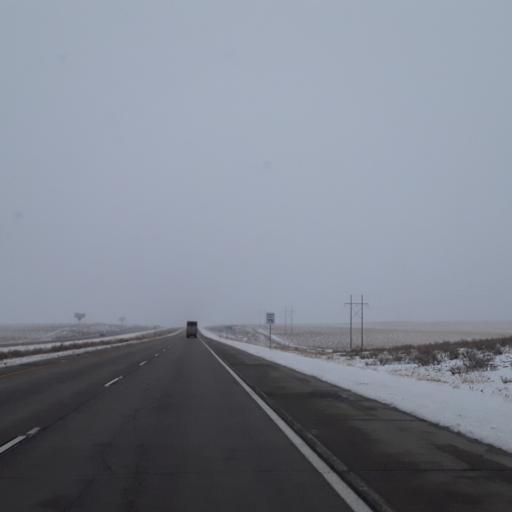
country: US
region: Colorado
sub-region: Logan County
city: Sterling
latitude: 40.7138
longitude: -103.0460
